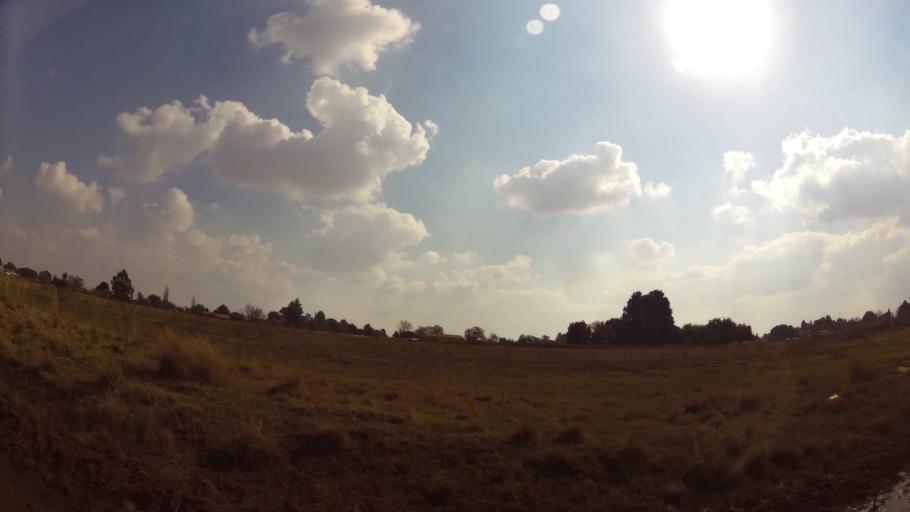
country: ZA
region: Mpumalanga
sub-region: Nkangala District Municipality
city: Delmas
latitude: -26.1576
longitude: 28.5551
